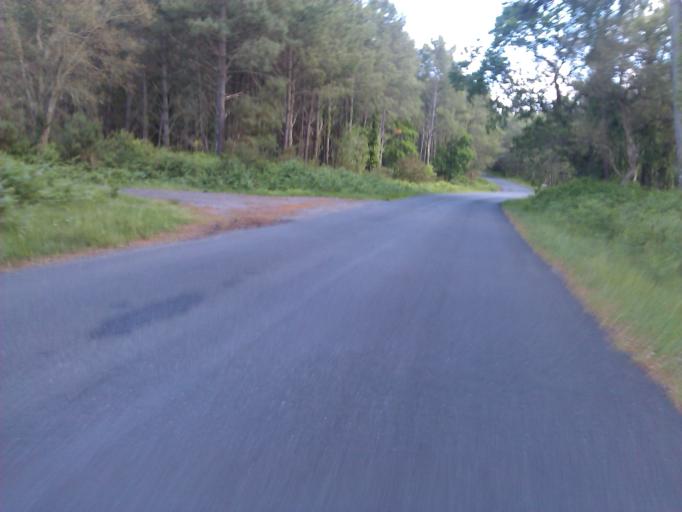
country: FR
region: Aquitaine
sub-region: Departement des Landes
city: Leon
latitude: 43.8711
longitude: -1.3623
